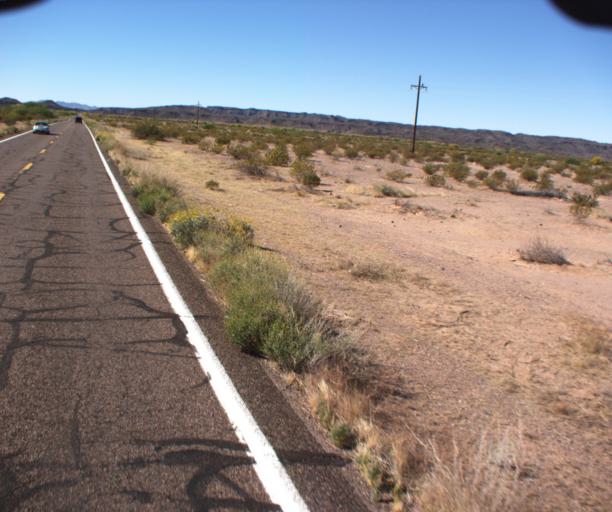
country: US
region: Arizona
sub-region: Pima County
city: Ajo
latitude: 32.5948
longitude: -112.8713
